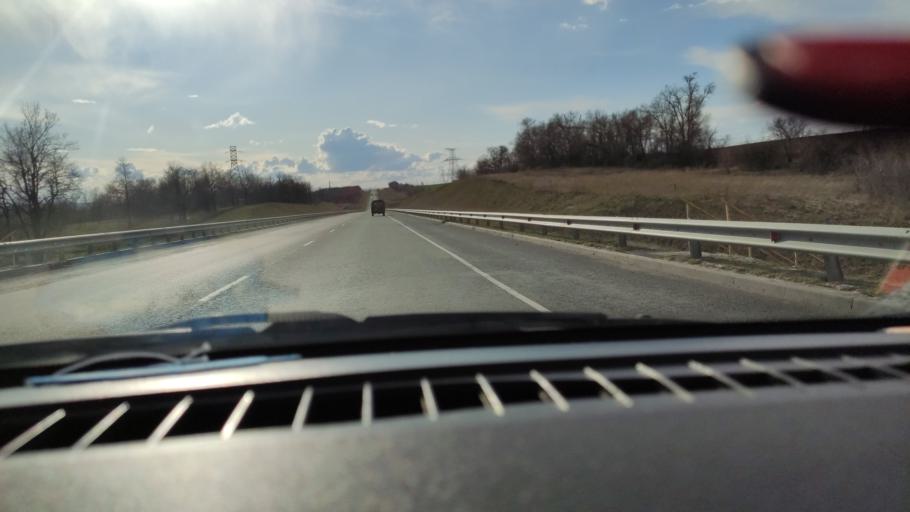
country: RU
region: Saratov
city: Yelshanka
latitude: 51.8226
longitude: 46.3220
